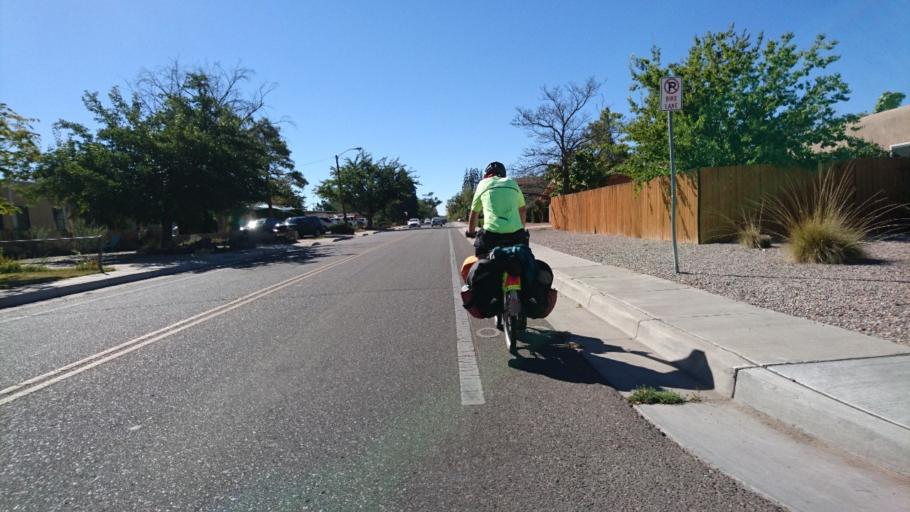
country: US
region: New Mexico
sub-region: Bernalillo County
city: Albuquerque
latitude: 35.0851
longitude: -106.5954
